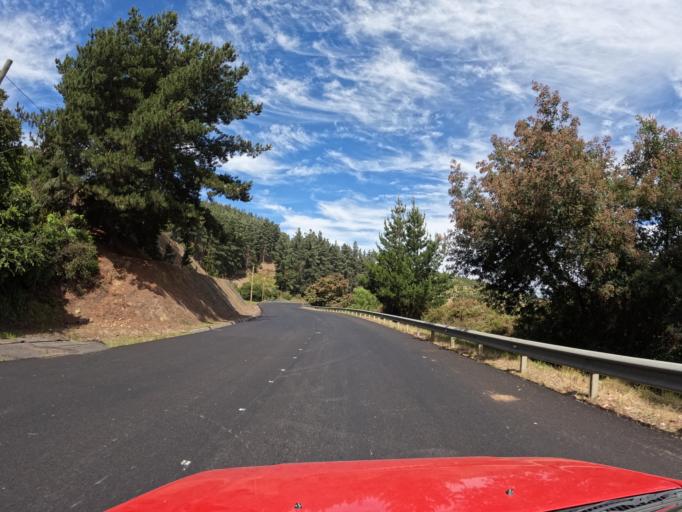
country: CL
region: Maule
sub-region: Provincia de Talca
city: Constitucion
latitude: -35.0494
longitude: -72.0469
